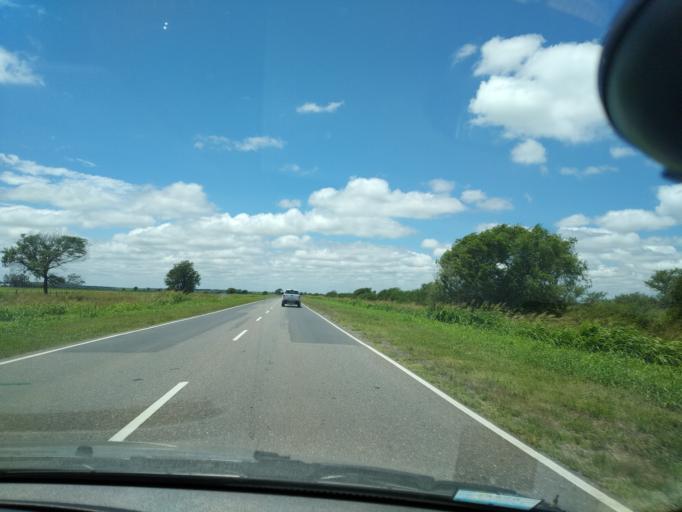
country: AR
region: Cordoba
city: Despenaderos
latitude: -31.6514
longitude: -64.1952
